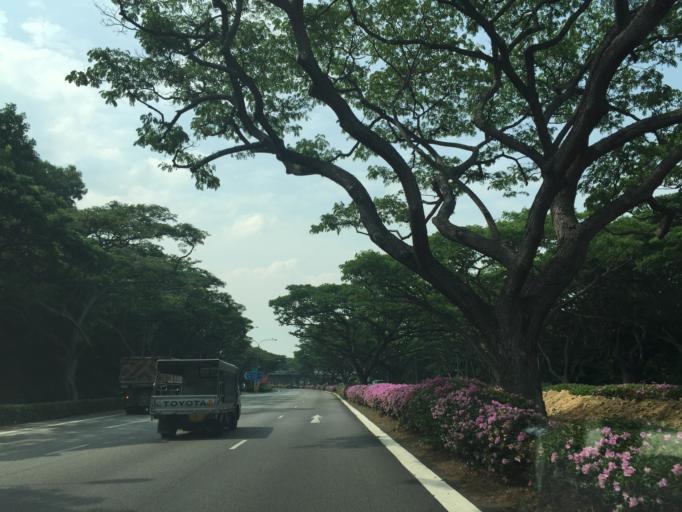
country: SG
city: Singapore
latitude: 1.3346
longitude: 103.9785
